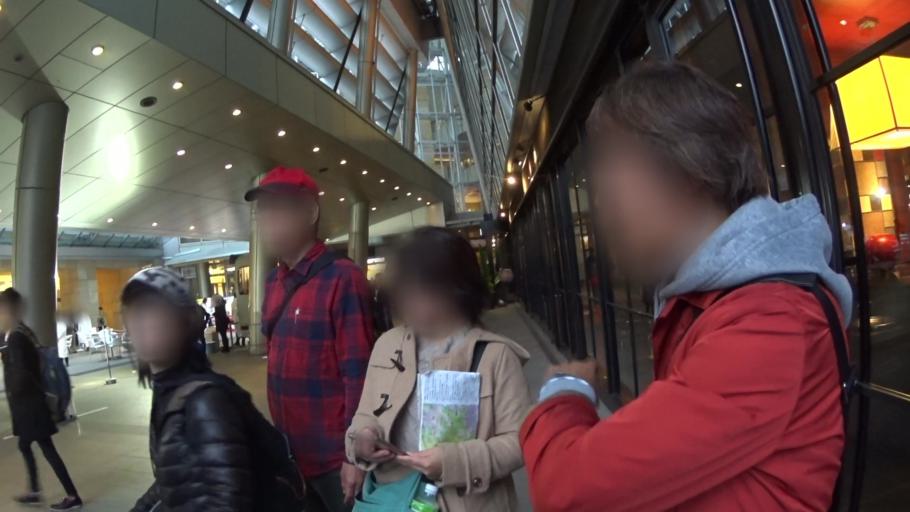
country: JP
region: Tokyo
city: Tokyo
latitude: 35.6599
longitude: 139.7294
